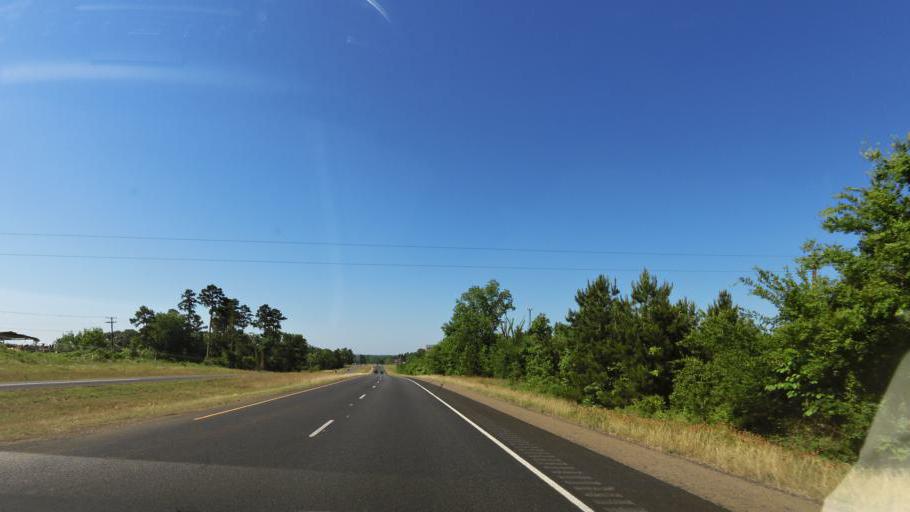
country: US
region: Texas
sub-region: Angelina County
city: Redland
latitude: 31.4894
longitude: -94.7190
